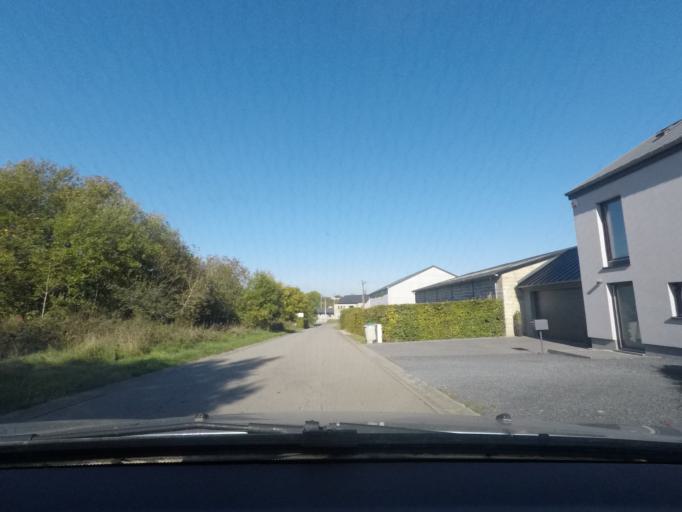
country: BE
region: Wallonia
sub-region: Province du Luxembourg
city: Habay-la-Vieille
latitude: 49.7175
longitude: 5.5654
